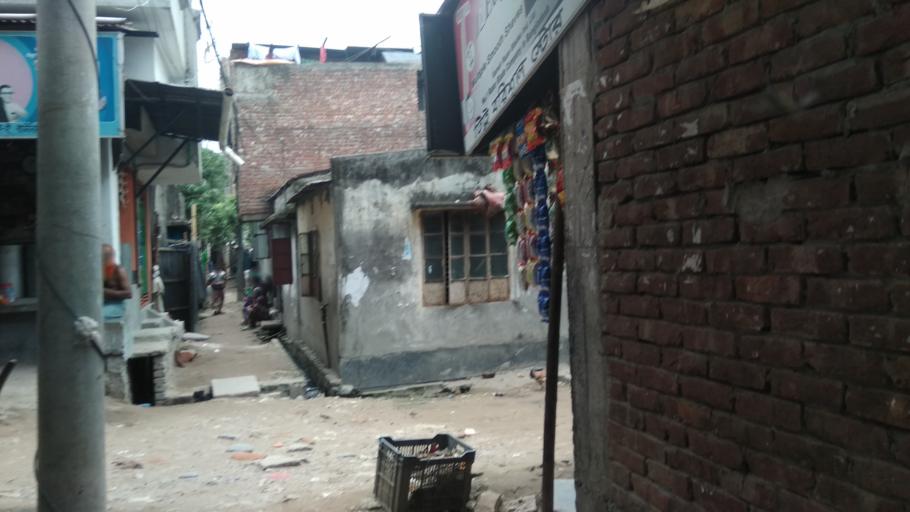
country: BD
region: Dhaka
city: Tungi
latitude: 23.8197
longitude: 90.3818
